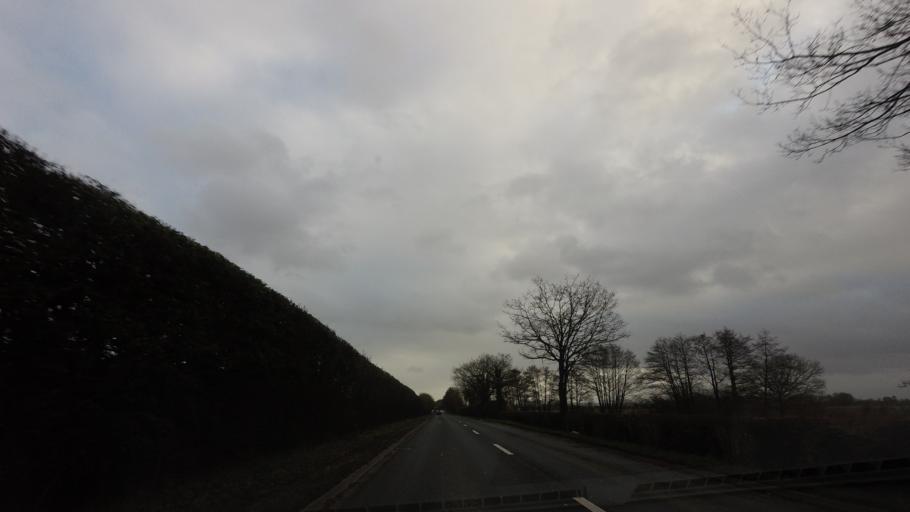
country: GB
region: England
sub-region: Kent
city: East Peckham
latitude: 51.2304
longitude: 0.3867
